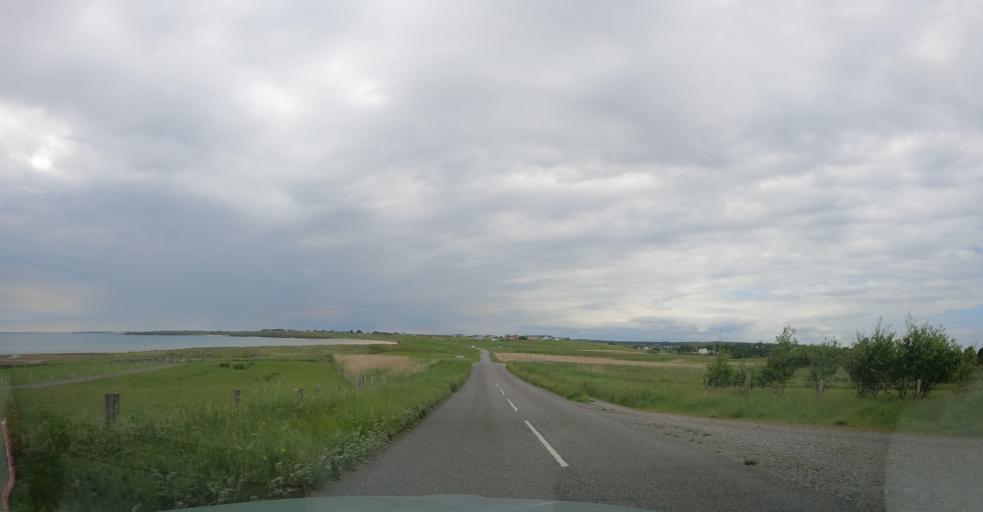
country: GB
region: Scotland
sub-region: Eilean Siar
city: Isle of Lewis
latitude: 58.2716
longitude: -6.3172
